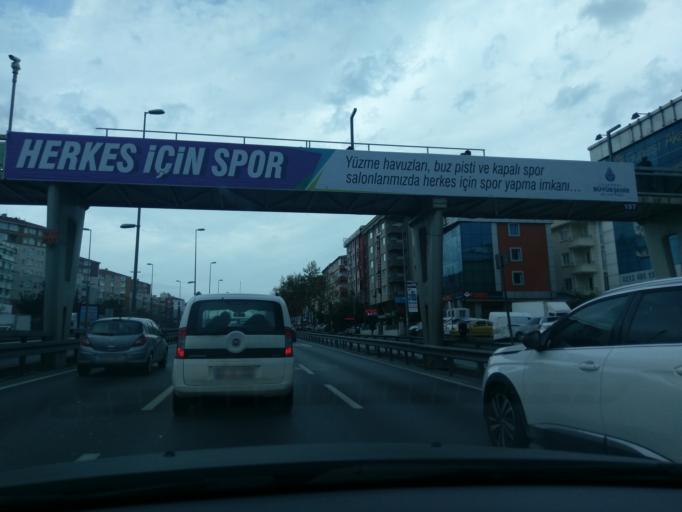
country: TR
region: Istanbul
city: Yakuplu
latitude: 40.9804
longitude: 28.7316
